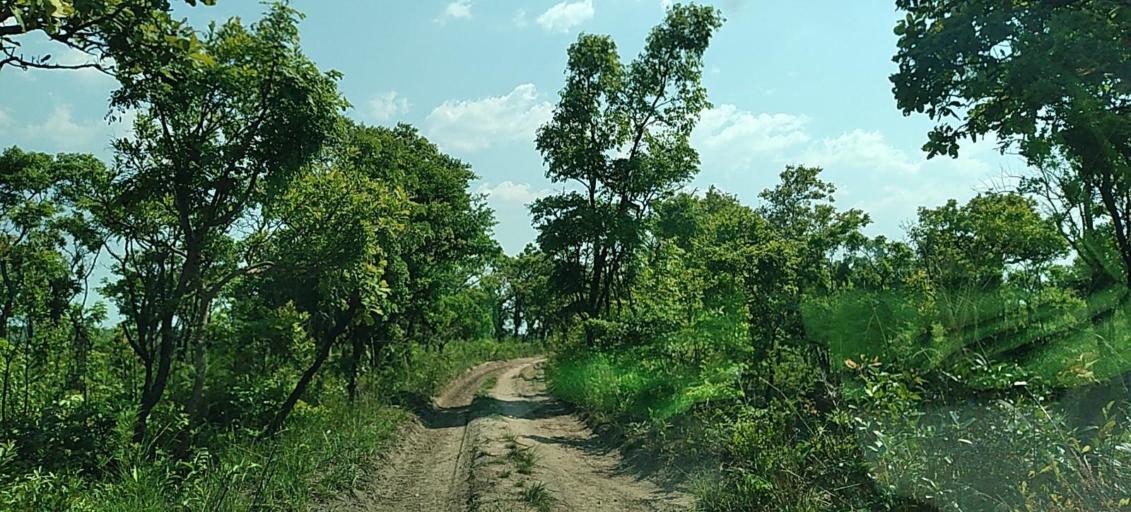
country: CD
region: Katanga
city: Kolwezi
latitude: -11.2597
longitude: 25.0100
